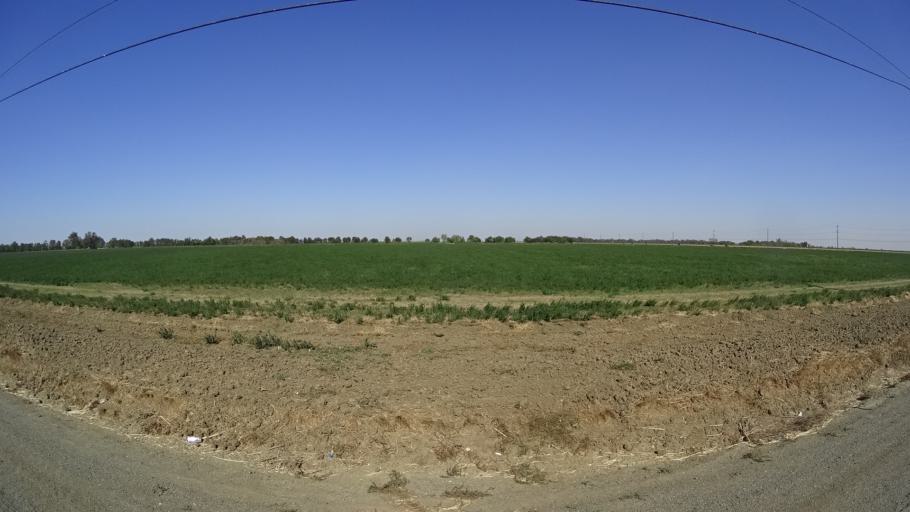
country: US
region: California
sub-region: Yolo County
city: Woodland
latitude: 38.6189
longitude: -121.7324
